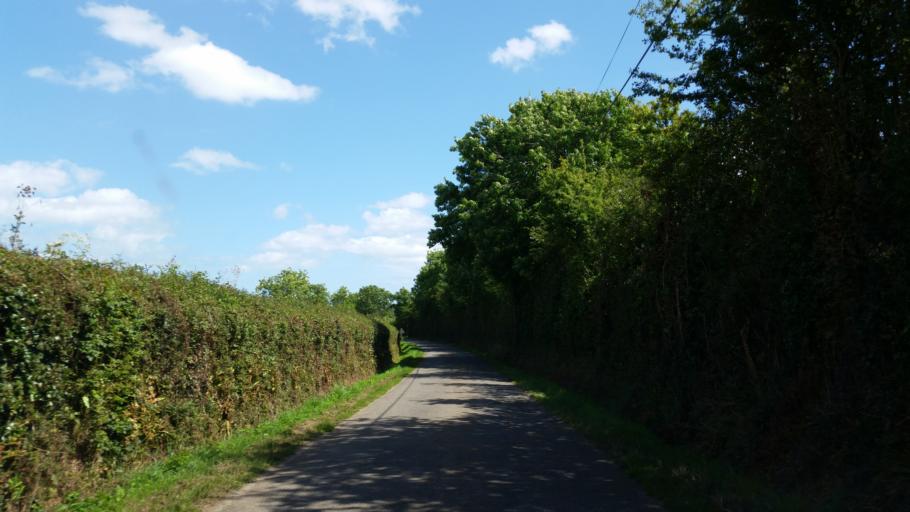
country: FR
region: Lower Normandy
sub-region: Departement de la Manche
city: Sainte-Mere-Eglise
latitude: 49.4596
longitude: -1.3260
